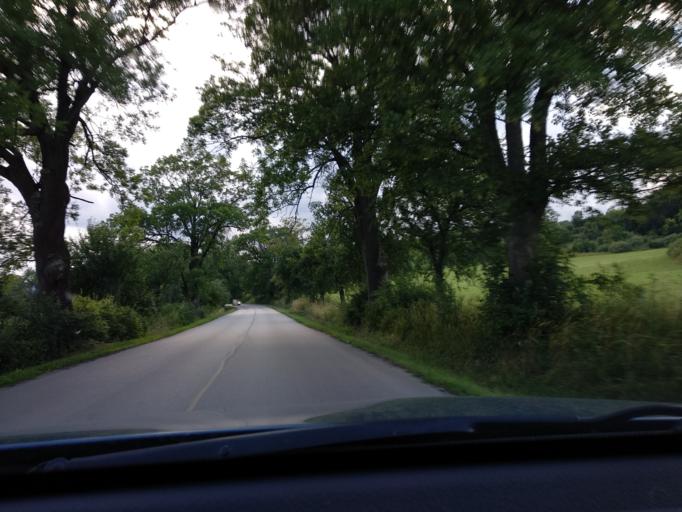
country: SK
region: Zilinsky
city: Ruzomberok
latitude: 49.1007
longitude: 19.4001
